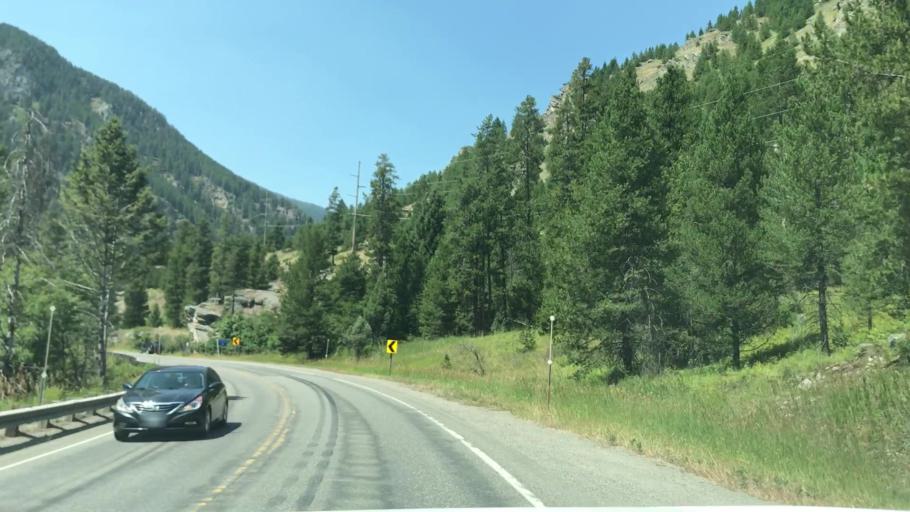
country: US
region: Montana
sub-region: Gallatin County
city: Big Sky
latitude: 45.3902
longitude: -111.1990
